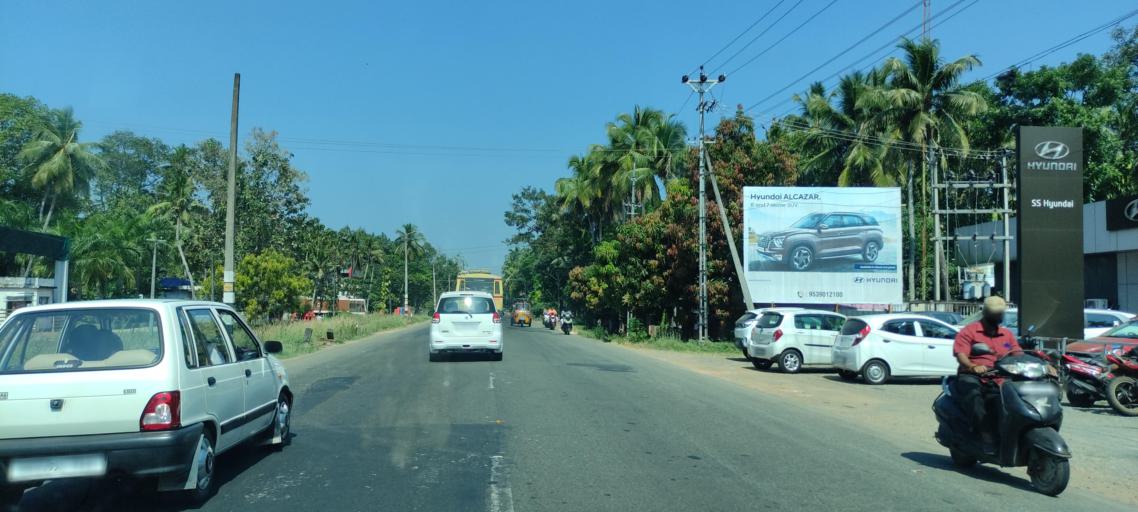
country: IN
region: Kerala
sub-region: Alappuzha
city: Kayankulam
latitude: 9.2044
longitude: 76.4833
